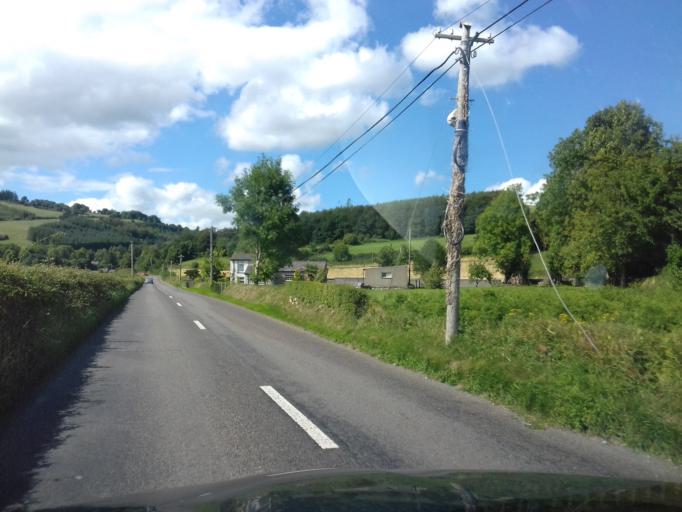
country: IE
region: Munster
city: Carrick-on-Suir
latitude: 52.3992
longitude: -7.4769
